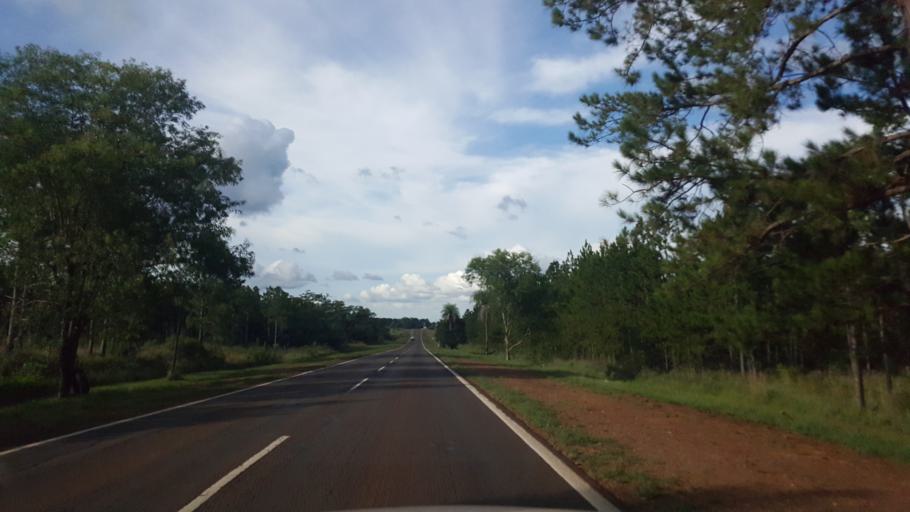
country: AR
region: Misiones
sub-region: Departamento de Candelaria
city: Loreto
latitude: -27.3438
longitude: -55.5463
